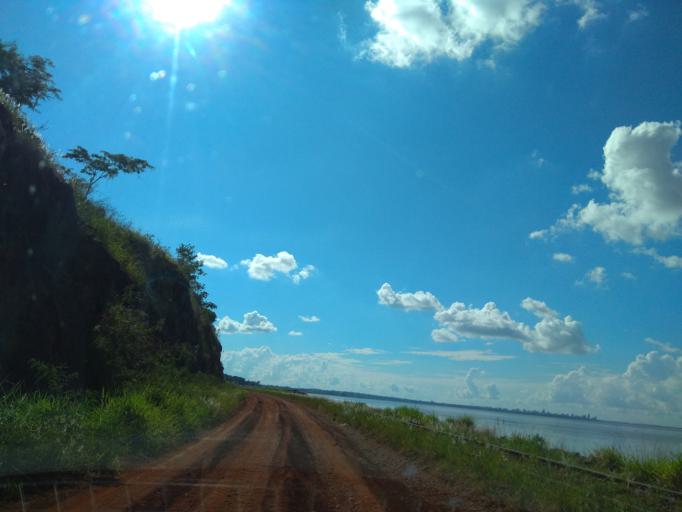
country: AR
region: Misiones
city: Garupa
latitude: -27.4460
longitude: -55.8420
